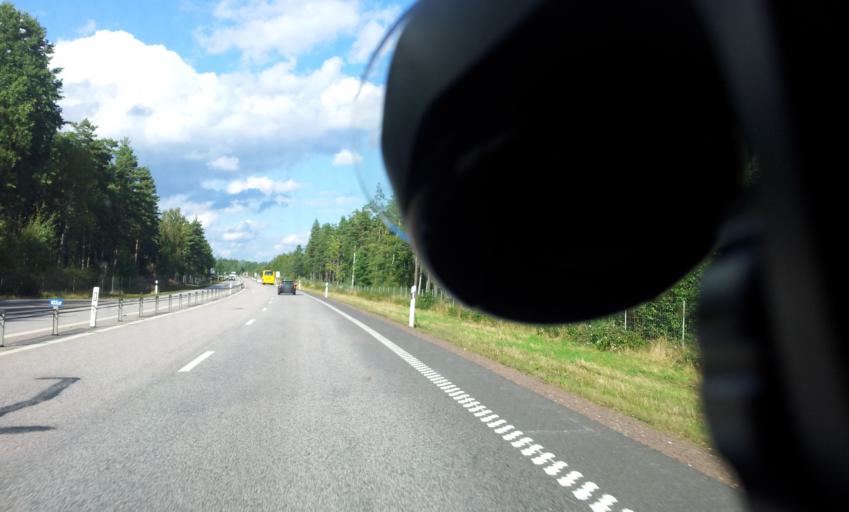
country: SE
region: Kalmar
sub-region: Oskarshamns Kommun
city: Paskallavik
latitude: 57.1060
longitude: 16.4988
